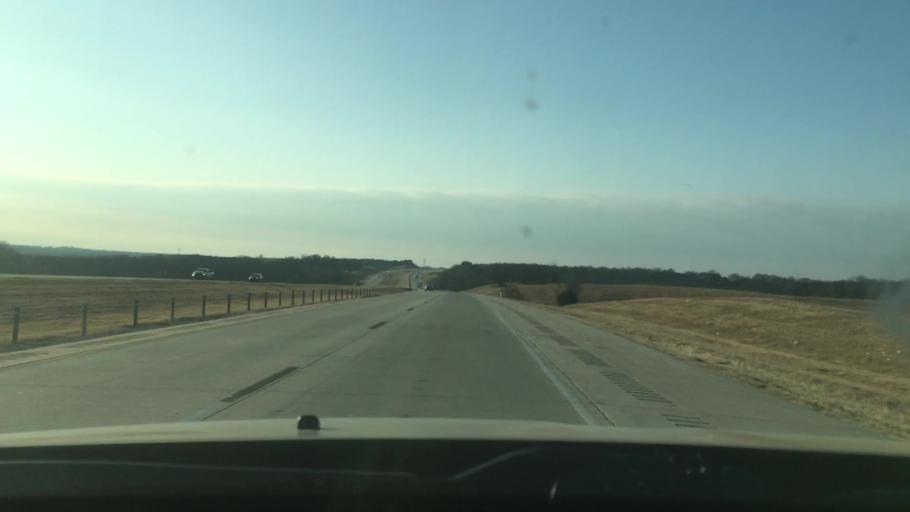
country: US
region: Oklahoma
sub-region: Carter County
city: Ardmore
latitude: 34.2517
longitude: -97.1649
